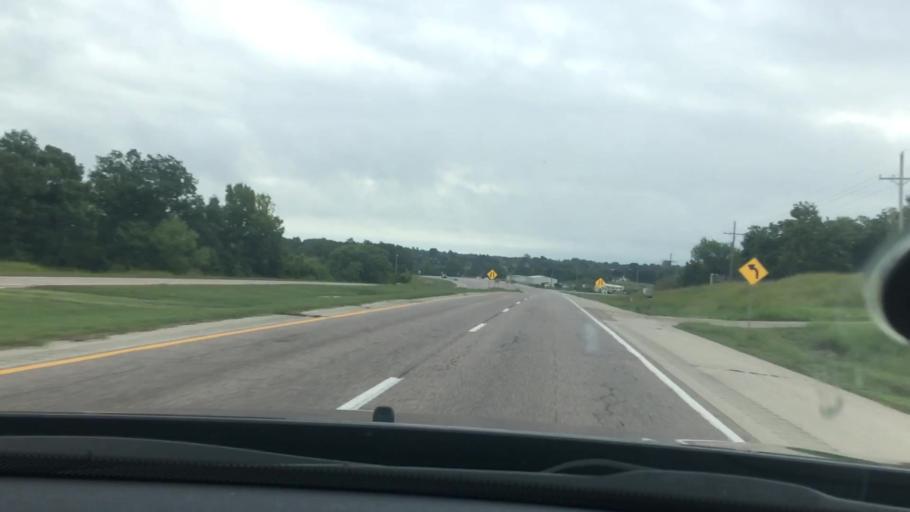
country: US
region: Oklahoma
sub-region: Pontotoc County
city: Ada
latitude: 34.7778
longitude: -96.5895
